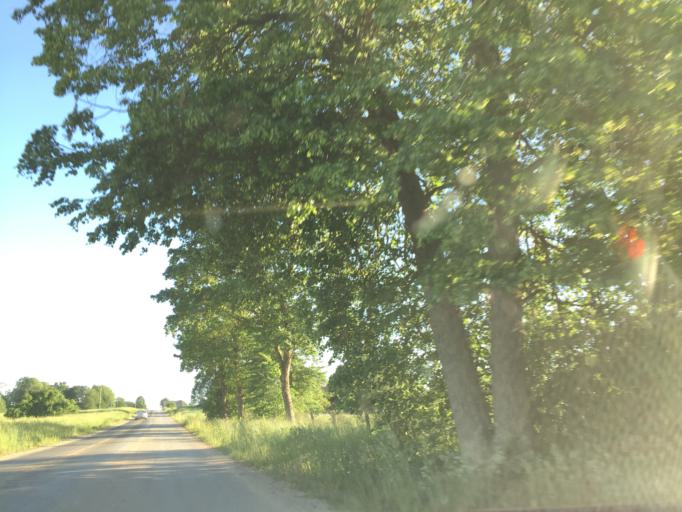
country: LV
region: Broceni
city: Broceni
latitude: 56.7770
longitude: 22.5397
